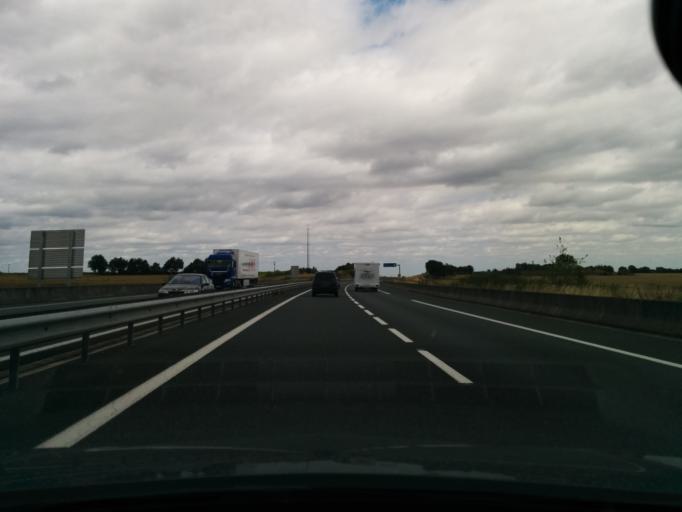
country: FR
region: Centre
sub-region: Departement de l'Indre
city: Argenton-sur-Creuse
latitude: 46.5418
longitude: 1.5070
